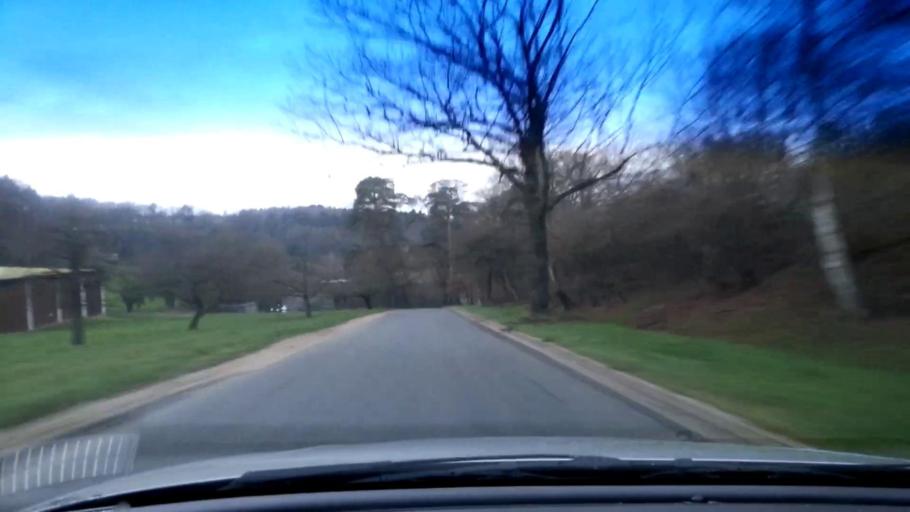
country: DE
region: Bavaria
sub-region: Upper Franconia
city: Viereth-Trunstadt
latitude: 49.9152
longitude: 10.7822
